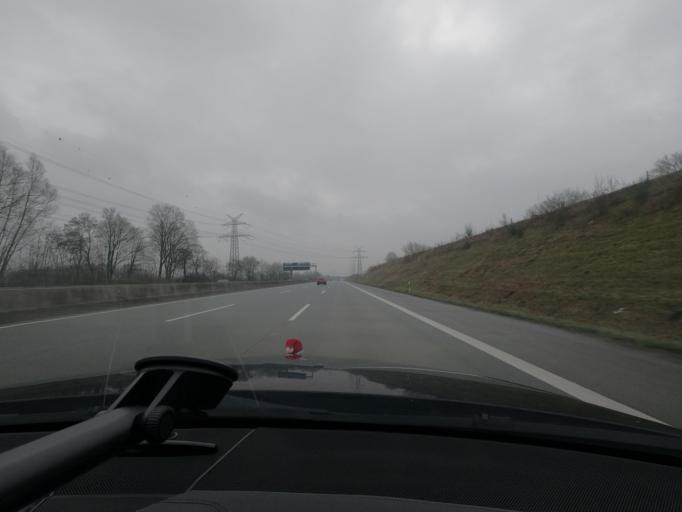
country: DE
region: Schleswig-Holstein
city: Alveslohe
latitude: 53.7970
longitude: 9.9325
